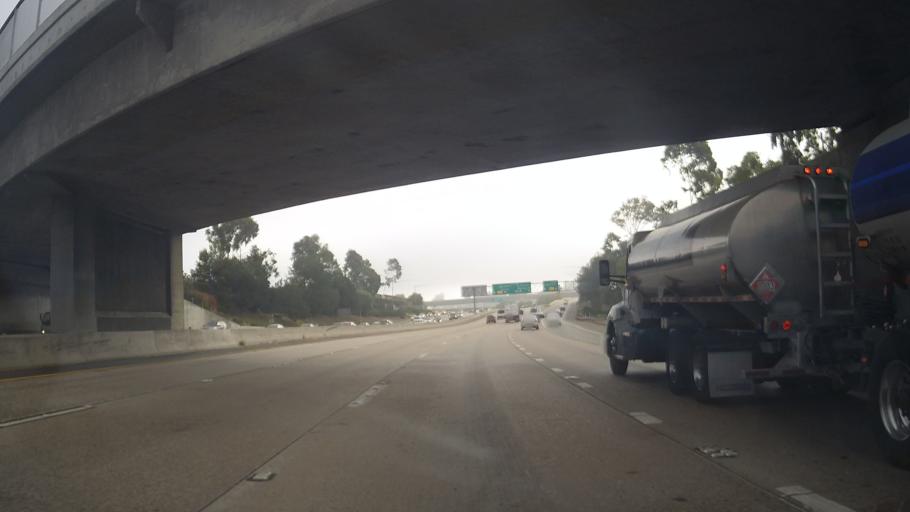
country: US
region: California
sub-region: San Diego County
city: Lemon Grove
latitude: 32.7484
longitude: -117.0273
